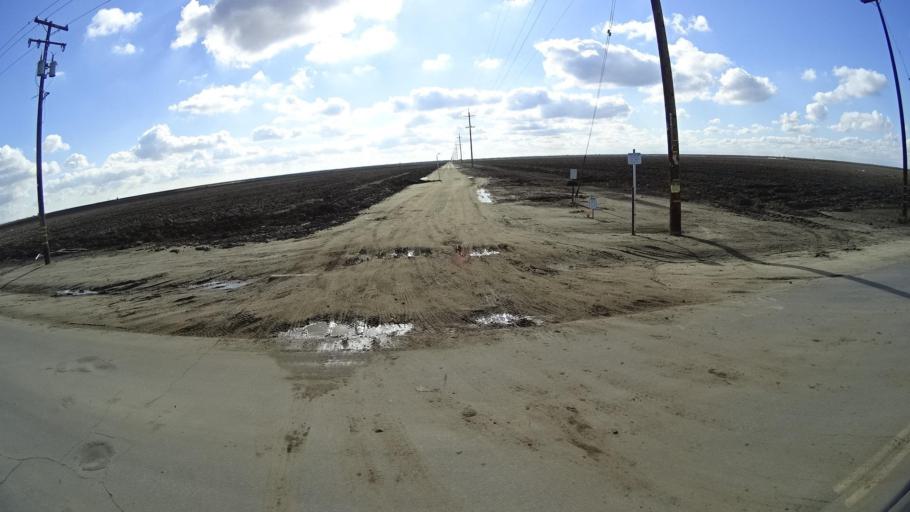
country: US
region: California
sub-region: Kern County
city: McFarland
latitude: 35.6743
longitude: -119.2765
